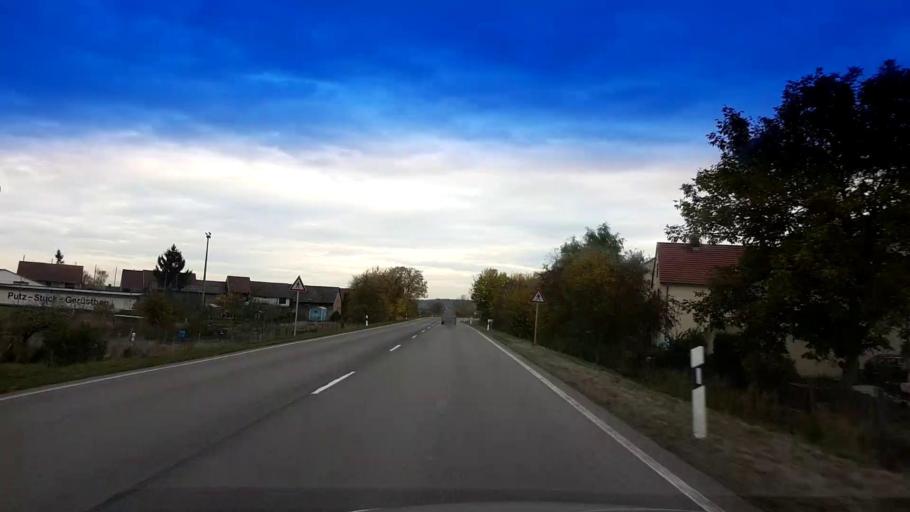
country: DE
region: Bavaria
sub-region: Regierungsbezirk Unterfranken
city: Stettfeld
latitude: 49.9482
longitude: 10.7230
